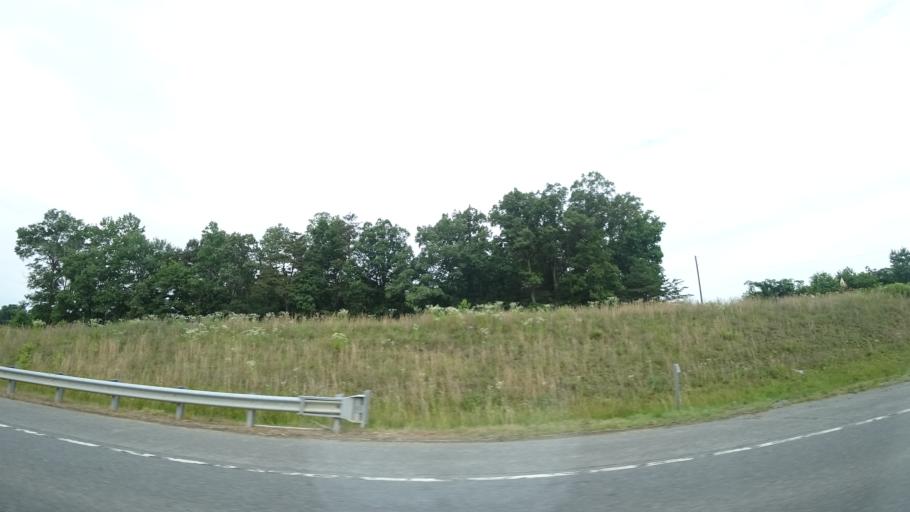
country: US
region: Virginia
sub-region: Spotsylvania County
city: Spotsylvania Courthouse
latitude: 38.1664
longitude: -77.6377
